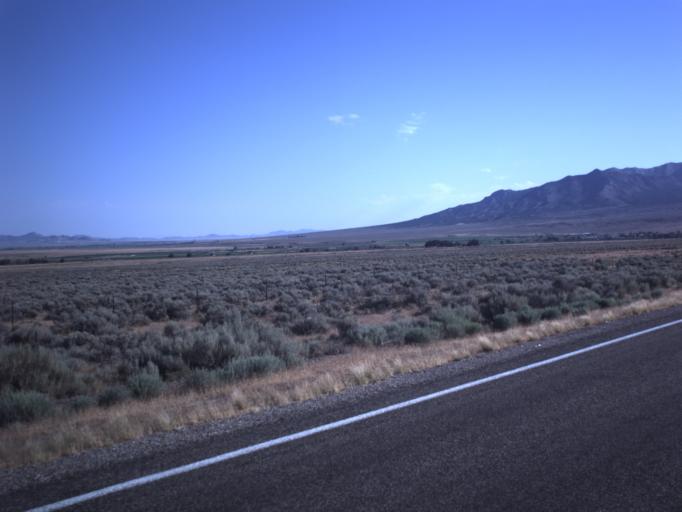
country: US
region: Utah
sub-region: Beaver County
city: Milford
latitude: 38.1802
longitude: -112.9457
